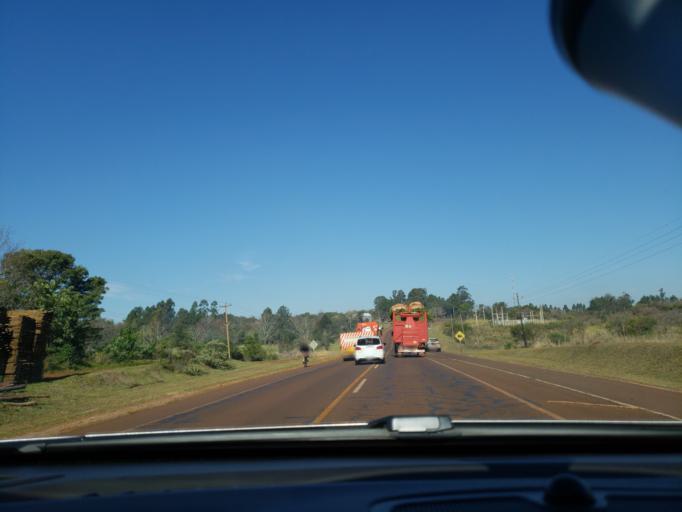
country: AR
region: Misiones
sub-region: Departamento de Apostoles
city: San Jose
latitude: -27.7590
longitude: -55.7735
